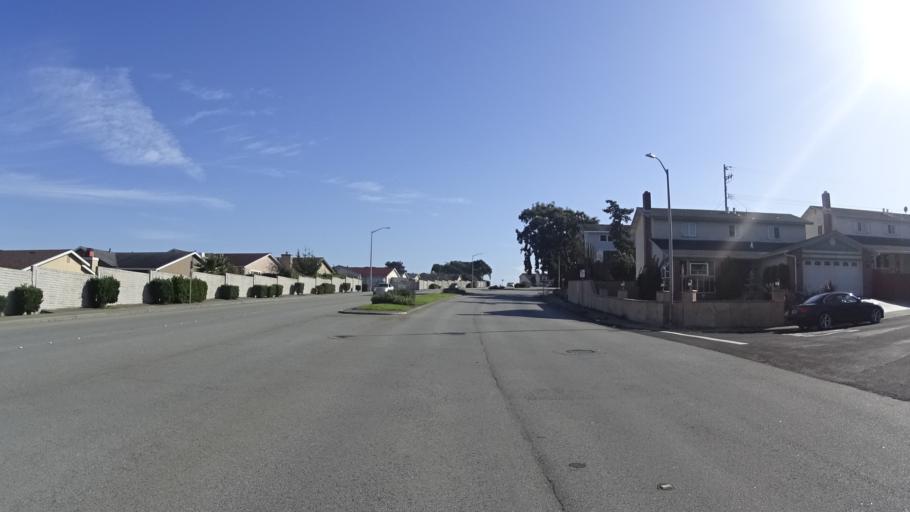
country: US
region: California
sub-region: San Mateo County
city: San Bruno
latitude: 37.6402
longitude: -122.4470
